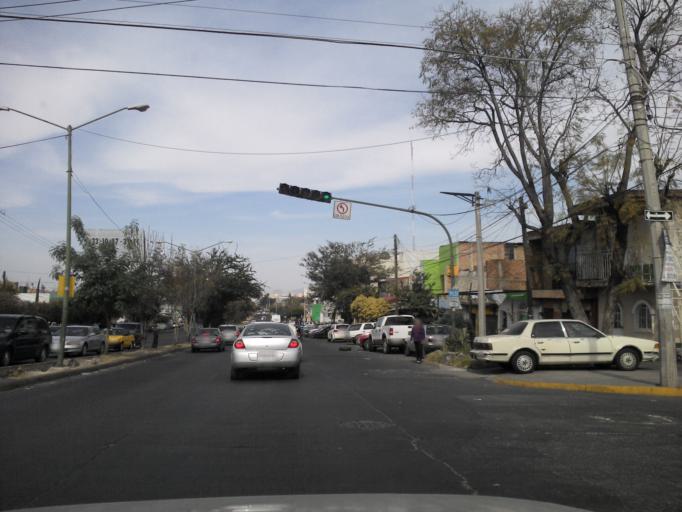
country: MX
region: Jalisco
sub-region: Tlajomulco de Zuniga
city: Altus Bosques
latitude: 20.6179
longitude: -103.3737
